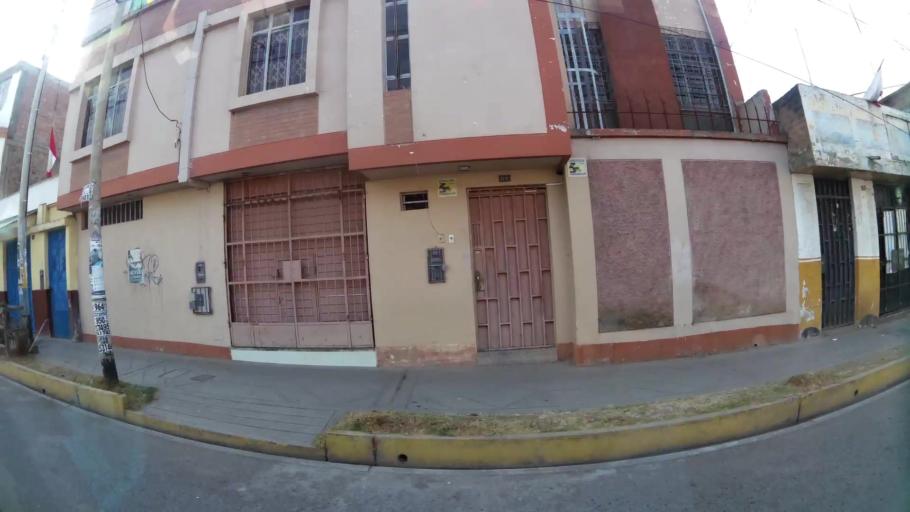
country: PE
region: Junin
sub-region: Provincia de Huancayo
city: Huancayo
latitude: -12.0538
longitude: -75.2027
